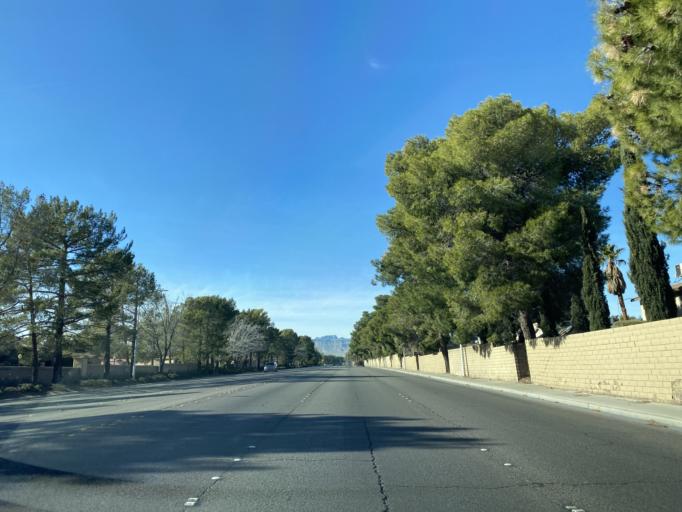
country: US
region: Nevada
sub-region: Clark County
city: Spring Valley
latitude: 36.0998
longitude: -115.2492
